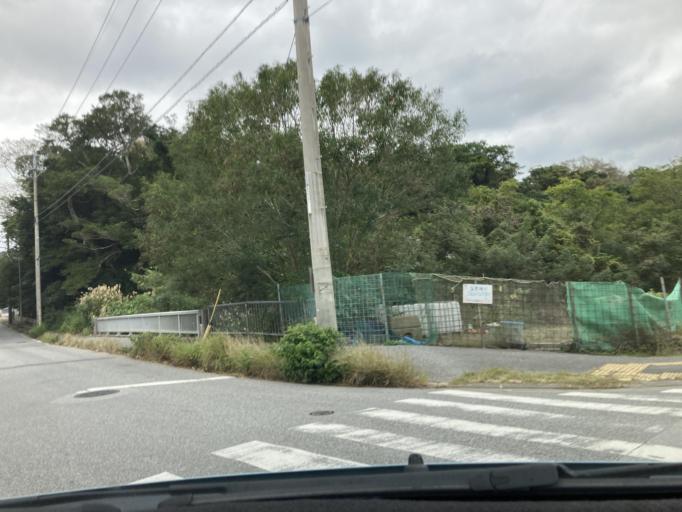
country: JP
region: Okinawa
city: Okinawa
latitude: 26.3465
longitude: 127.8077
